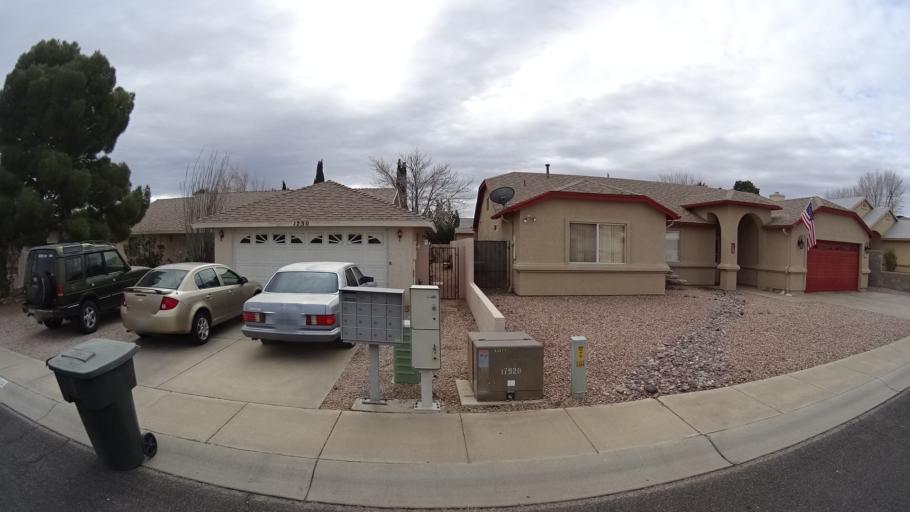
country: US
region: Arizona
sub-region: Mohave County
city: New Kingman-Butler
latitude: 35.2329
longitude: -114.0392
